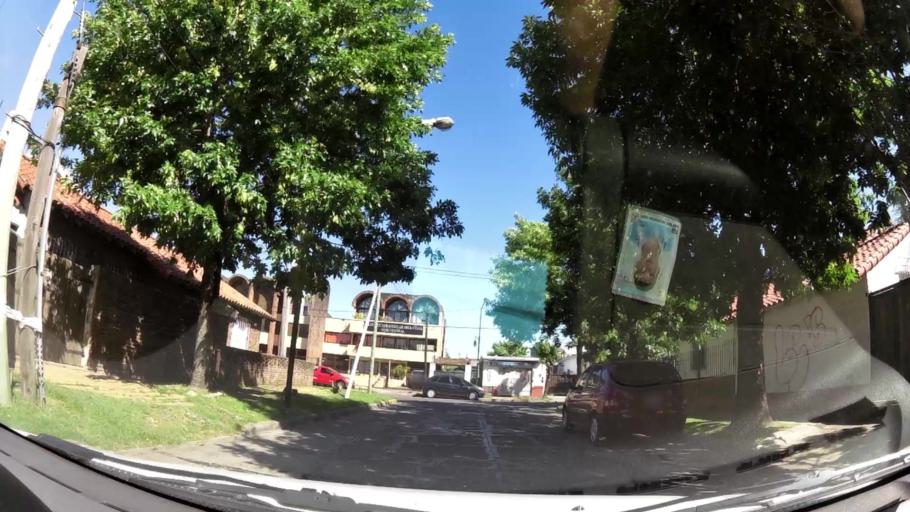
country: AR
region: Buenos Aires
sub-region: Partido de San Isidro
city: San Isidro
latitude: -34.4734
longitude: -58.5321
